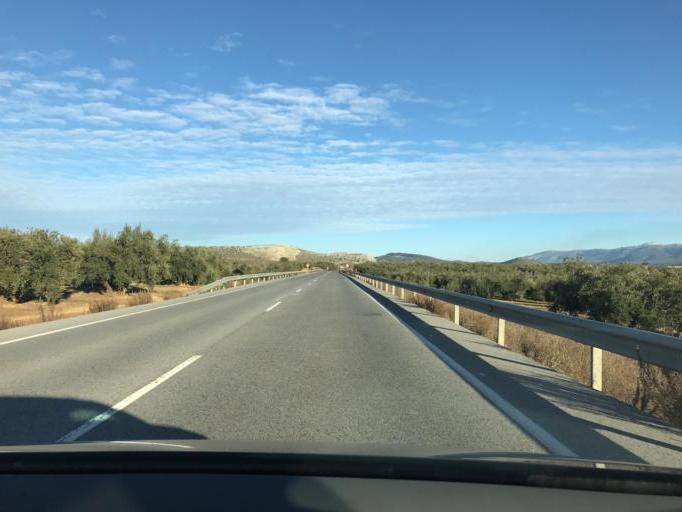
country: ES
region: Andalusia
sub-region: Provincia de Granada
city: Iznalloz
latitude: 37.4015
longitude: -3.5405
